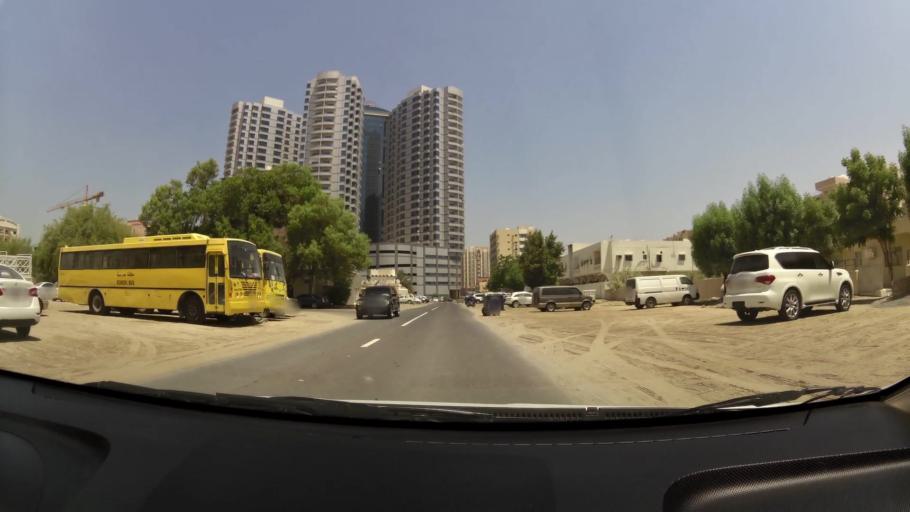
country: AE
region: Ajman
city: Ajman
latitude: 25.3978
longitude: 55.4505
